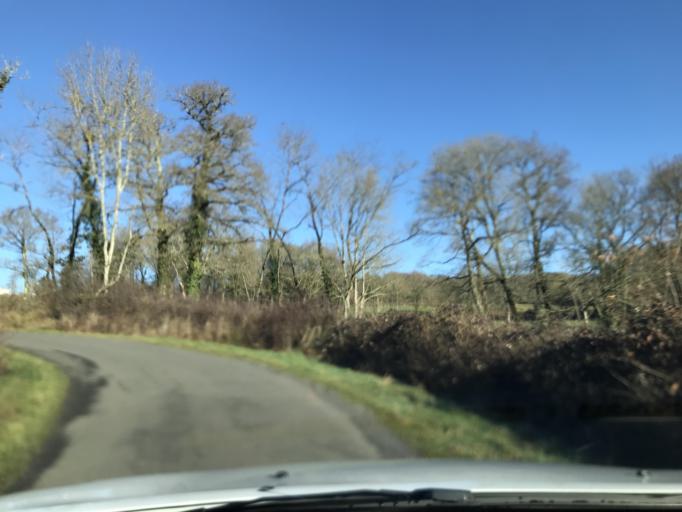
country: FR
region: Poitou-Charentes
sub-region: Departement de la Charente
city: Loubert
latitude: 45.8374
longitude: 0.5406
